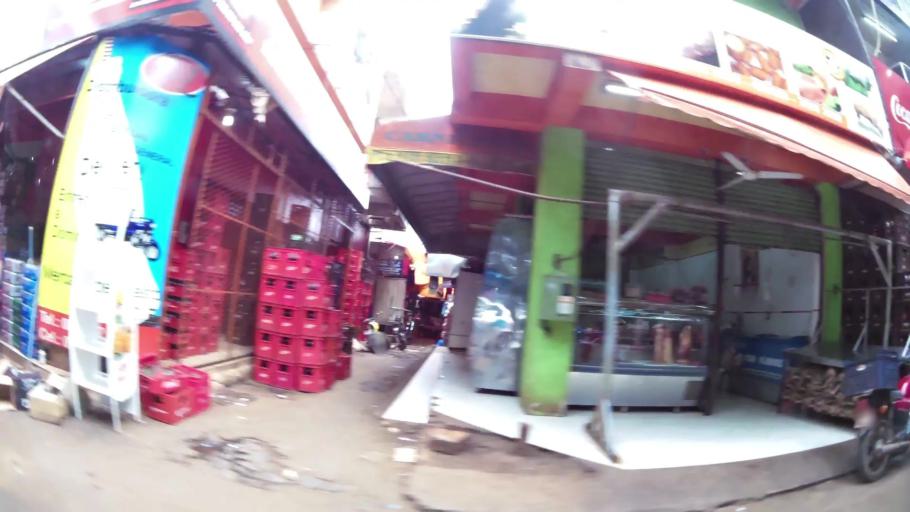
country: PY
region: Alto Parana
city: Presidente Franco
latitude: -25.5342
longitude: -54.6127
